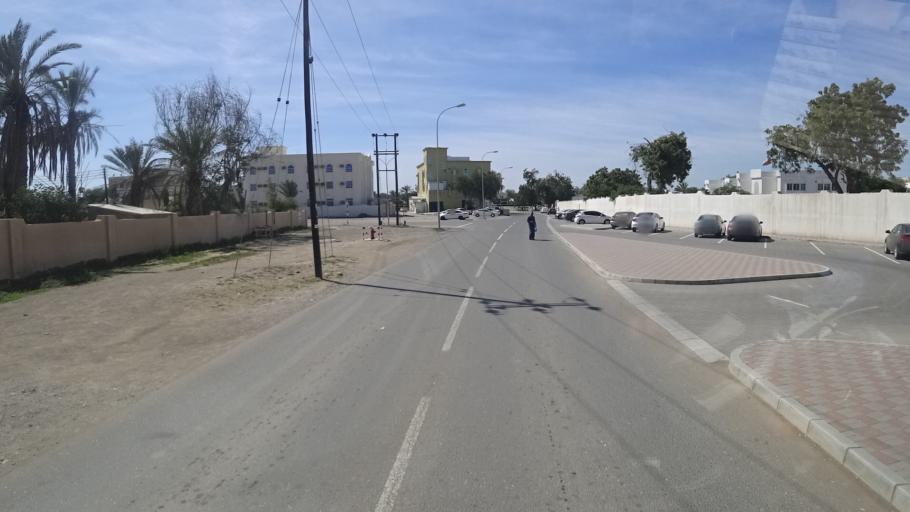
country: OM
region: Al Batinah
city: Al Sohar
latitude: 24.2934
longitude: 56.7835
